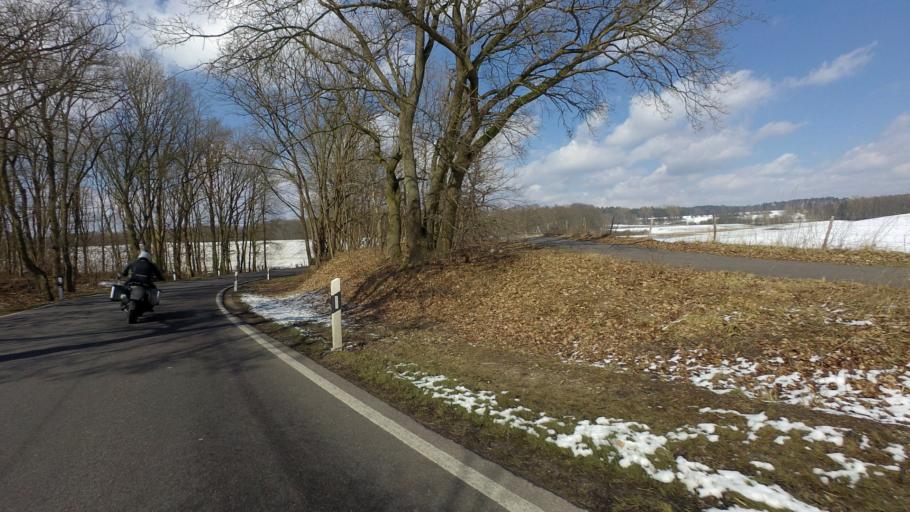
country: DE
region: Brandenburg
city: Britz
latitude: 52.8846
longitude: 13.7246
